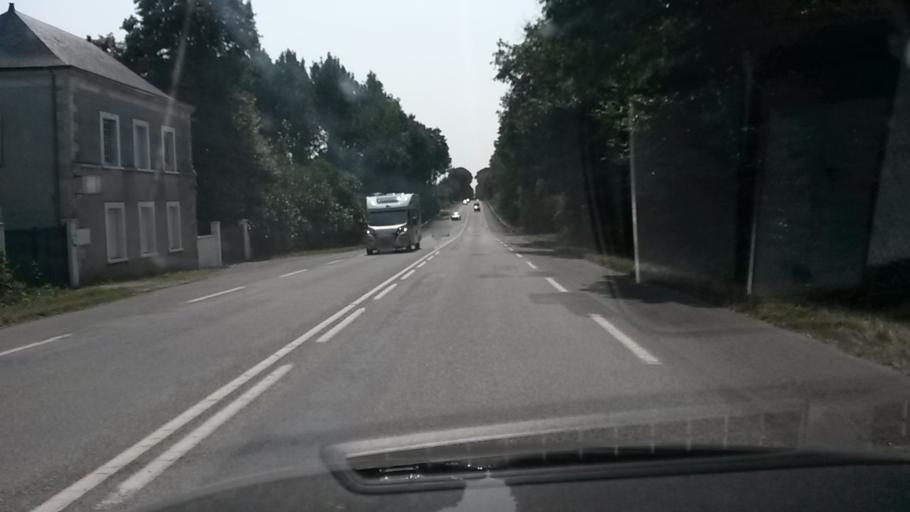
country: FR
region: Pays de la Loire
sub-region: Departement de la Mayenne
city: Chateau-Gontier
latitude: 47.8720
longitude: -0.6870
